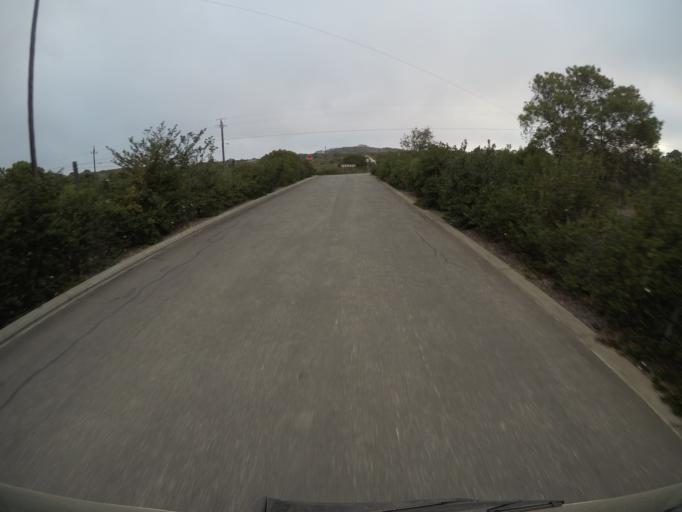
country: ZA
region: Western Cape
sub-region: Eden District Municipality
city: Mossel Bay
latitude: -34.1439
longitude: 22.0884
